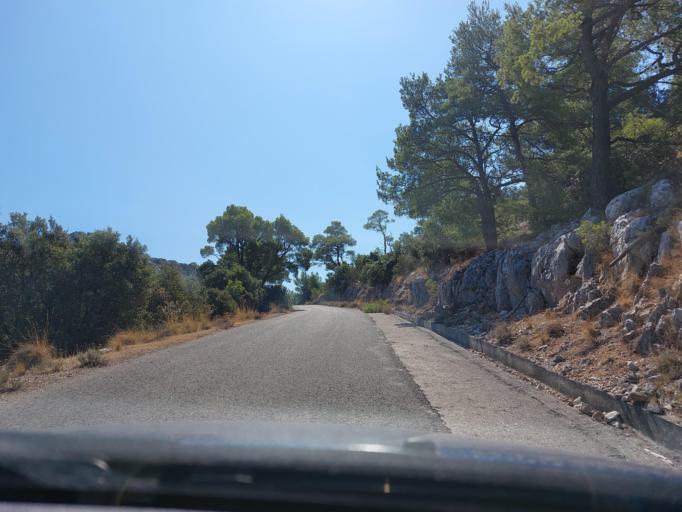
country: HR
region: Dubrovacko-Neretvanska
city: Smokvica
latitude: 42.7468
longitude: 16.8528
